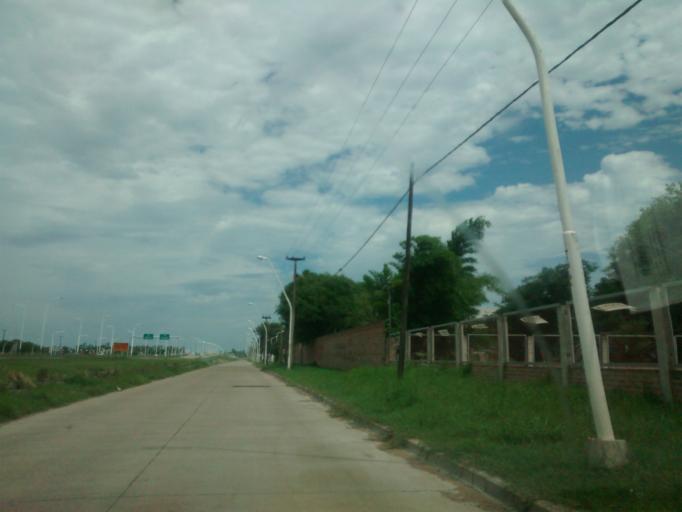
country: AR
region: Chaco
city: Resistencia
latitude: -27.4173
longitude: -58.9650
